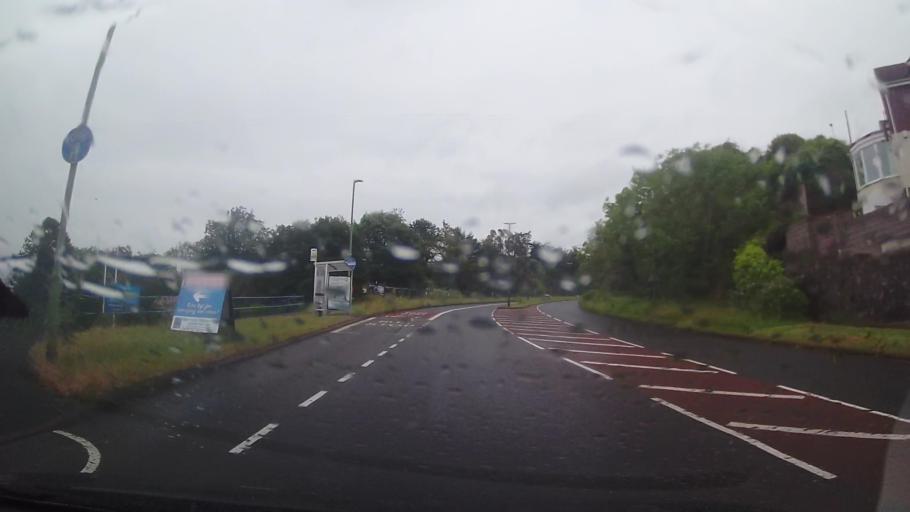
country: GB
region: England
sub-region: Borough of Torbay
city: Paignton
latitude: 50.4141
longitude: -3.5608
